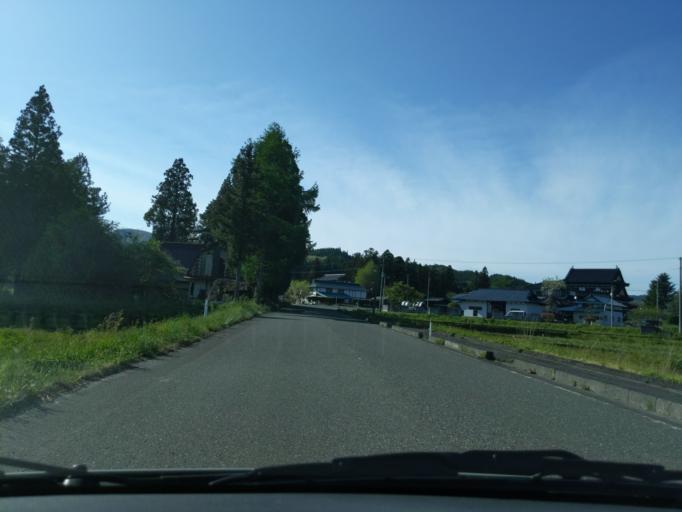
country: JP
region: Iwate
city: Ichinoseki
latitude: 38.8410
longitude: 140.9084
